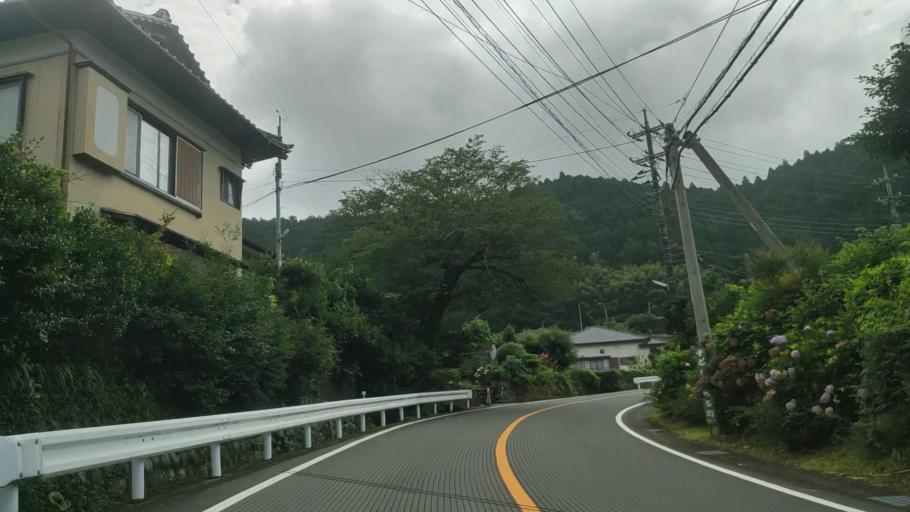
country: JP
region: Shizuoka
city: Fujinomiya
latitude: 35.2185
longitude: 138.5177
